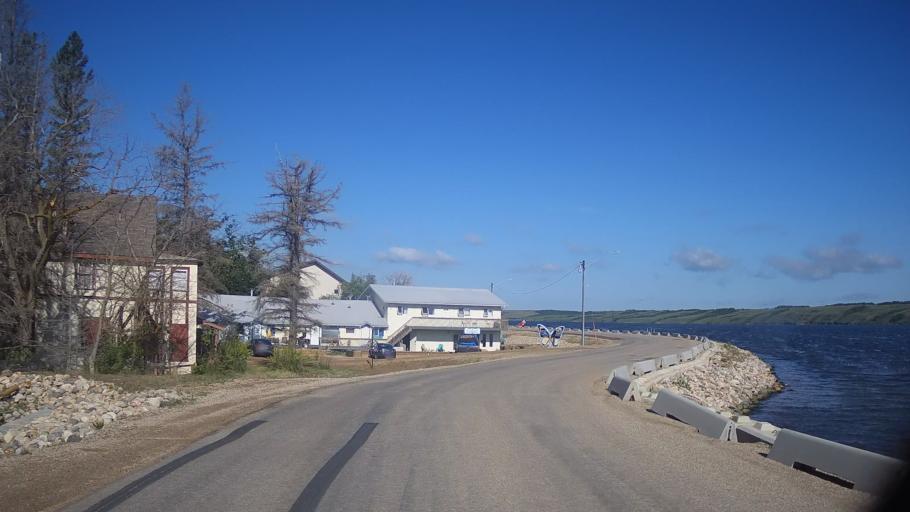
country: CA
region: Saskatchewan
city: Watrous
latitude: 51.7191
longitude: -105.4342
